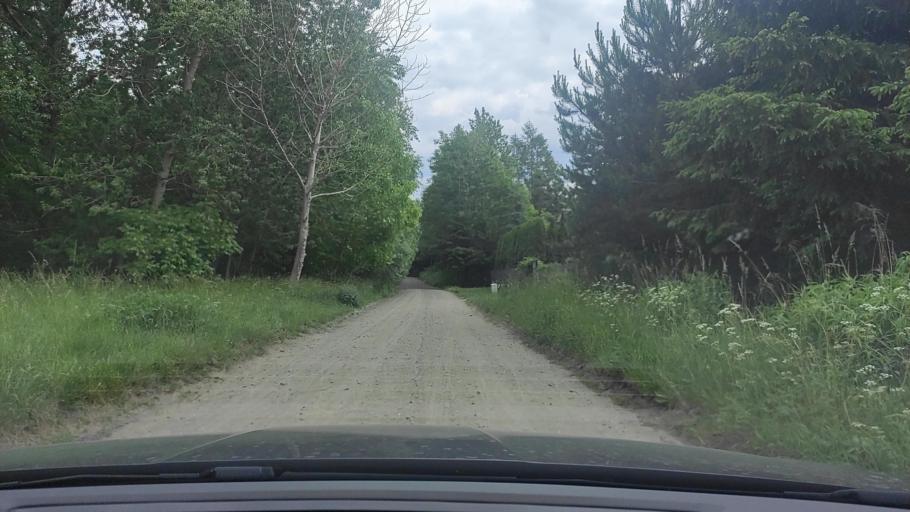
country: PL
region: Greater Poland Voivodeship
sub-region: Powiat poznanski
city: Pobiedziska
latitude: 52.4941
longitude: 17.1974
